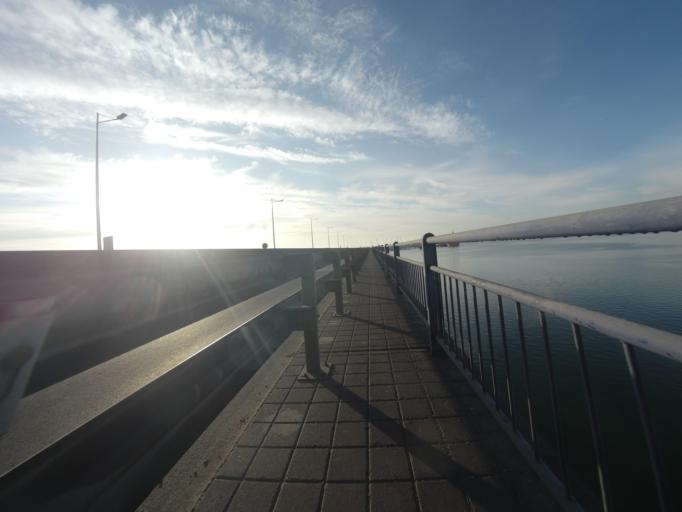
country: ES
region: Andalusia
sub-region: Provincia de Huelva
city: Punta Umbria
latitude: 37.2117
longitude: -6.9383
